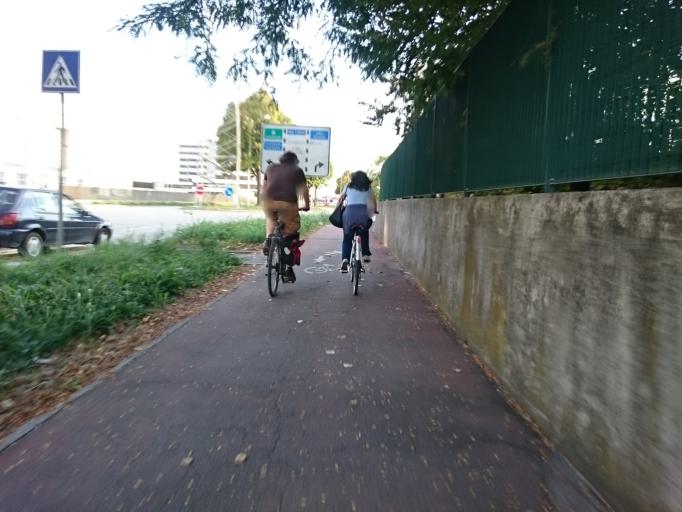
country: IT
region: Veneto
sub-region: Provincia di Padova
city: Noventa
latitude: 45.3941
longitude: 11.9454
